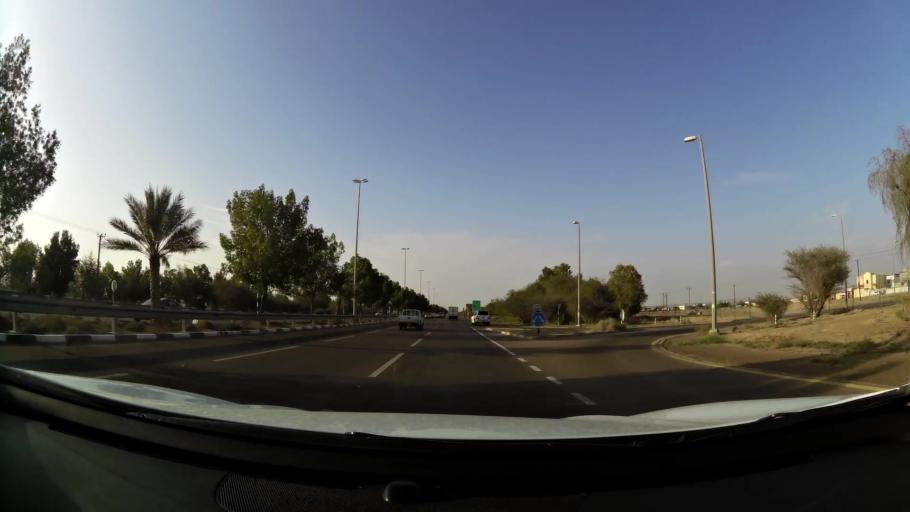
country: AE
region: Abu Dhabi
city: Al Ain
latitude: 24.1057
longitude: 55.8270
